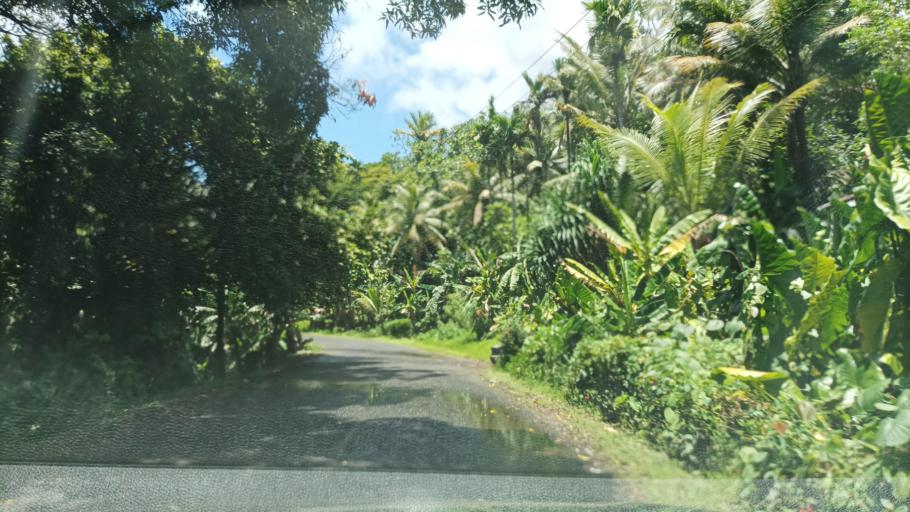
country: FM
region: Pohnpei
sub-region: Madolenihm Municipality
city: Madolenihm Municipality Government
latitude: 6.8544
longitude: 158.2962
